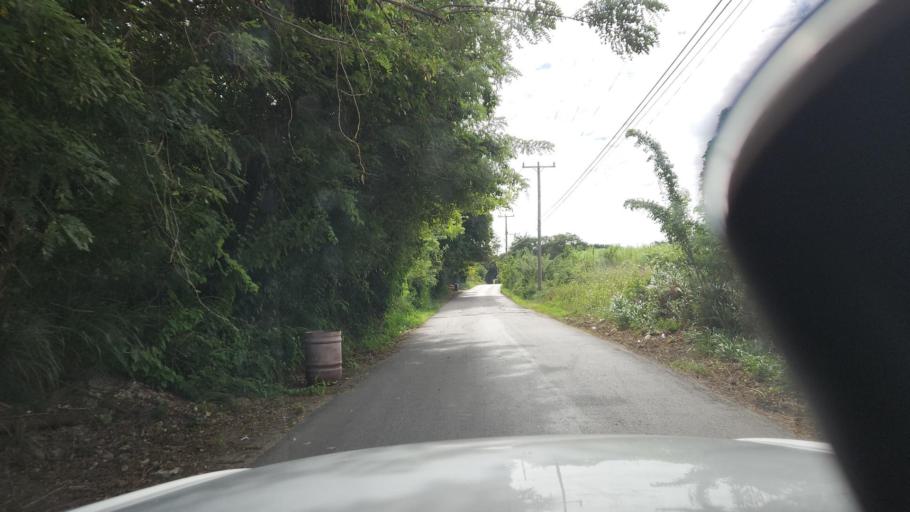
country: BB
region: Saint Lucy
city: Checker Hall
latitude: 13.2743
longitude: -59.6400
